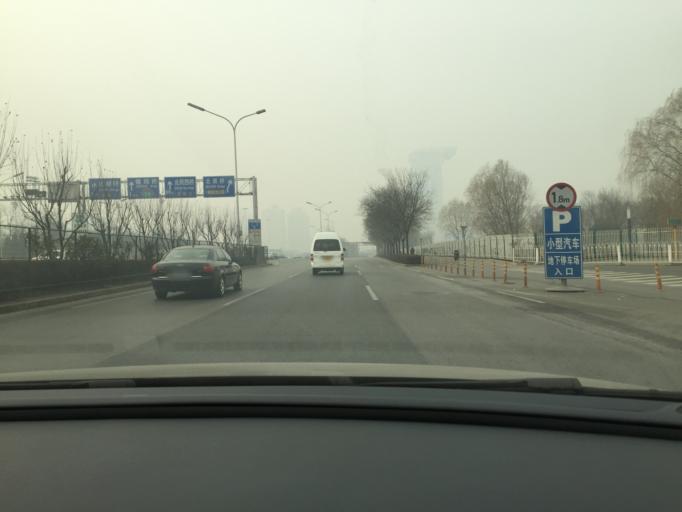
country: CN
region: Beijing
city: Datun
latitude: 39.9871
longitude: 116.3930
